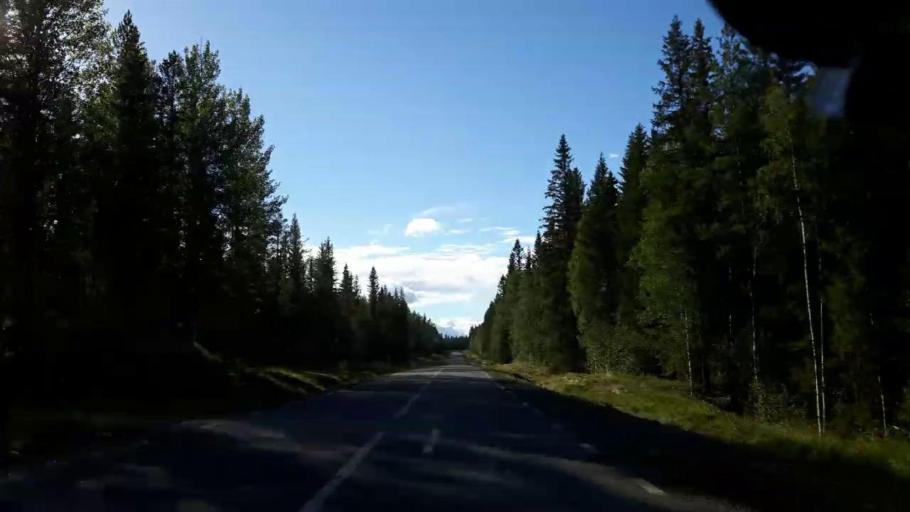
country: SE
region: Jaemtland
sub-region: Ragunda Kommun
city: Hammarstrand
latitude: 63.5374
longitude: 16.0125
